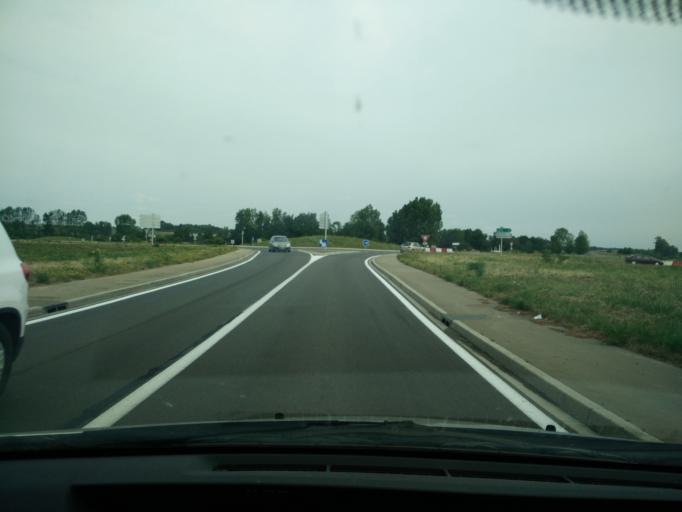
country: FR
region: Poitou-Charentes
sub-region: Departement des Deux-Sevres
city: Sainte-Verge
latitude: 47.0134
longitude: -0.2004
